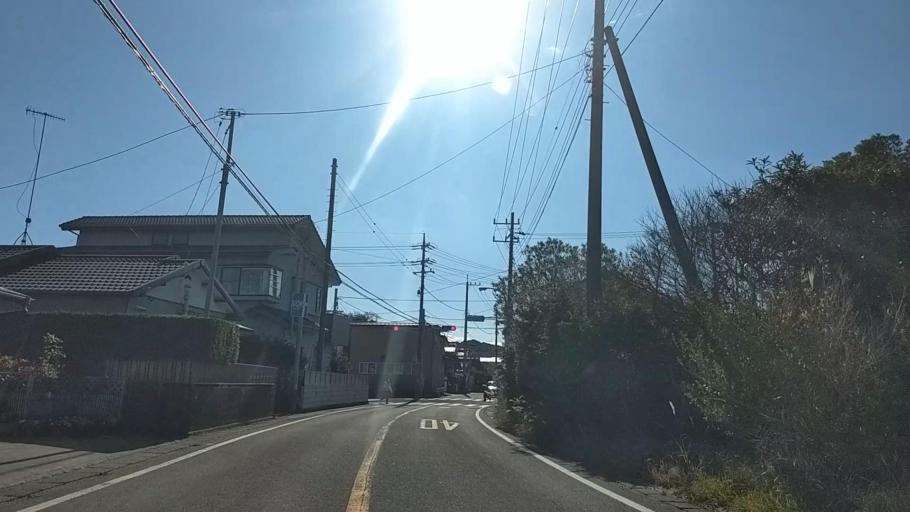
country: JP
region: Chiba
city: Tateyama
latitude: 34.9817
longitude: 139.8628
